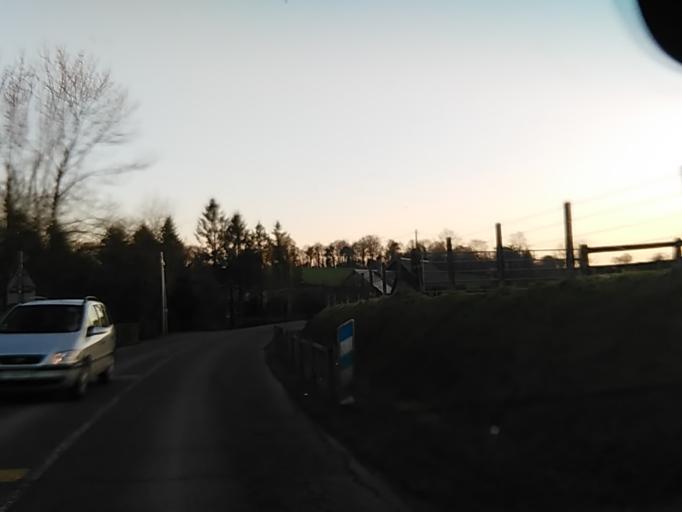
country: FR
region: Lower Normandy
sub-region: Departement de l'Orne
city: La Ferte-Mace
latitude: 48.6424
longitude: -0.3531
